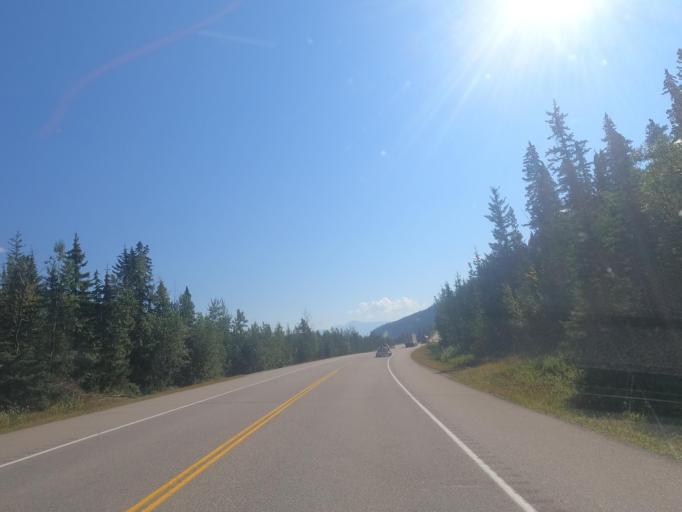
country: CA
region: Alberta
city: Jasper Park Lodge
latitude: 52.8762
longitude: -118.3177
